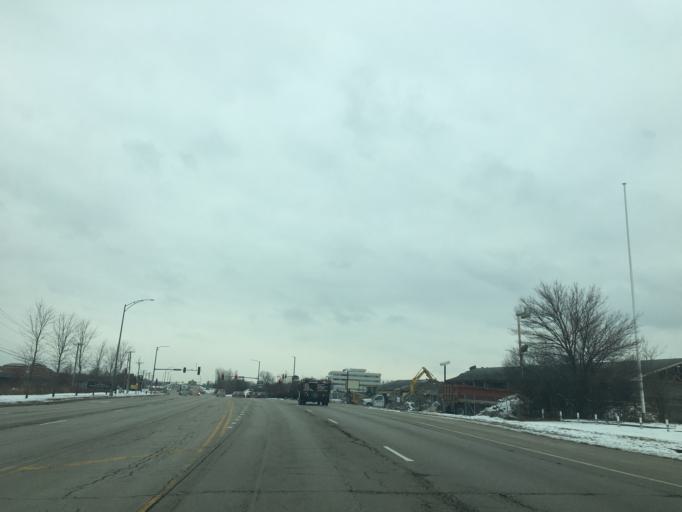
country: US
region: Illinois
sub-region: Kane County
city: North Aurora
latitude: 41.8058
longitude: -88.2820
